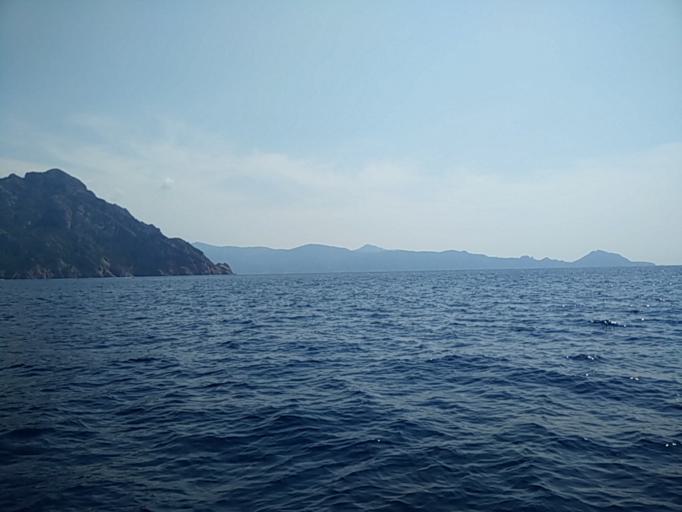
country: FR
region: Corsica
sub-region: Departement de la Corse-du-Sud
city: Cargese
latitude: 42.3411
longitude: 8.5838
